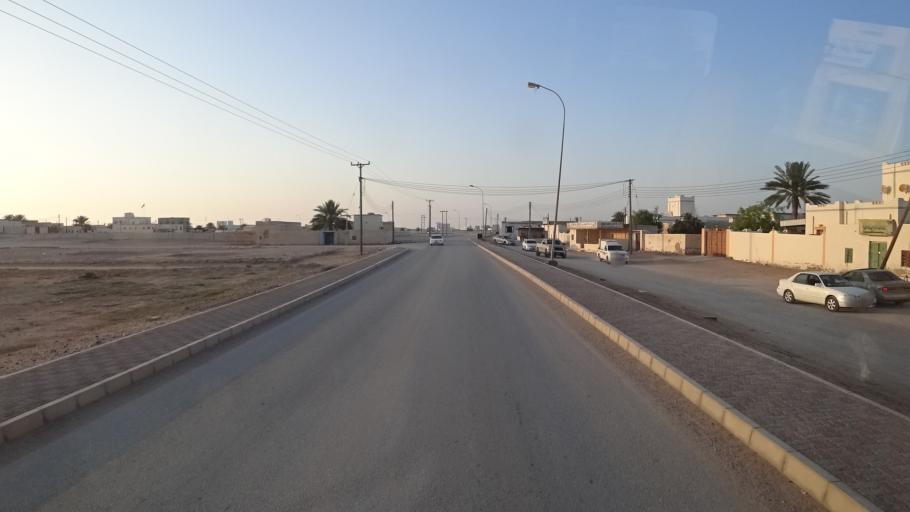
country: OM
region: Ash Sharqiyah
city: Sur
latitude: 22.5234
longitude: 59.7920
